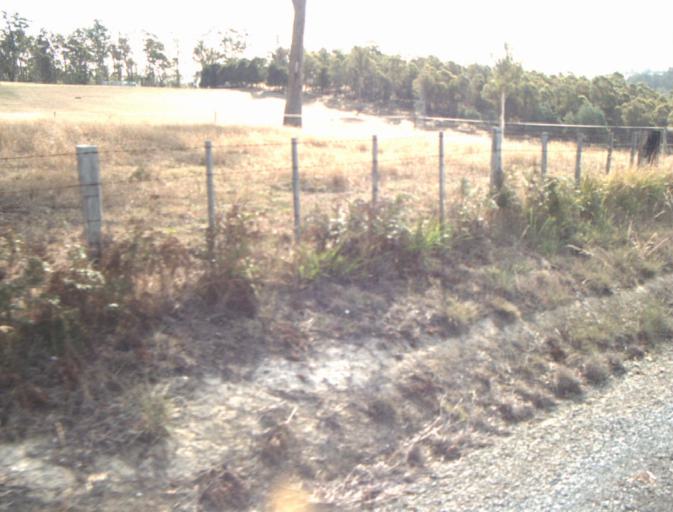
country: AU
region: Tasmania
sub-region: Launceston
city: Mayfield
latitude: -41.2141
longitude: 147.1350
